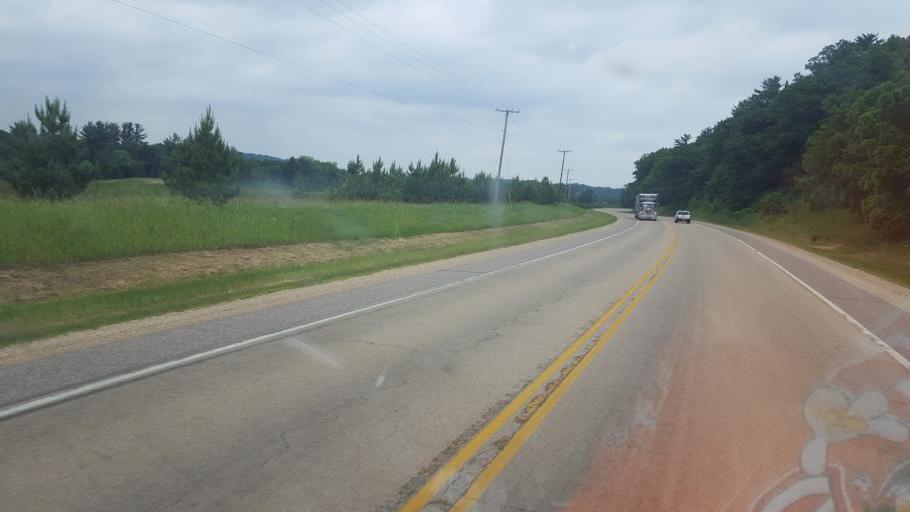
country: US
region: Wisconsin
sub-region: Juneau County
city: Elroy
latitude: 43.6345
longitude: -90.1760
